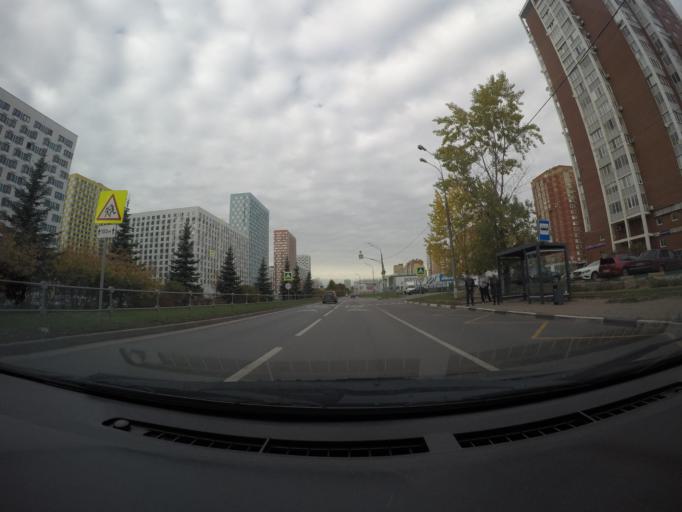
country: RU
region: Moskovskaya
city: Mytishchi
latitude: 55.9180
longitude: 37.7238
